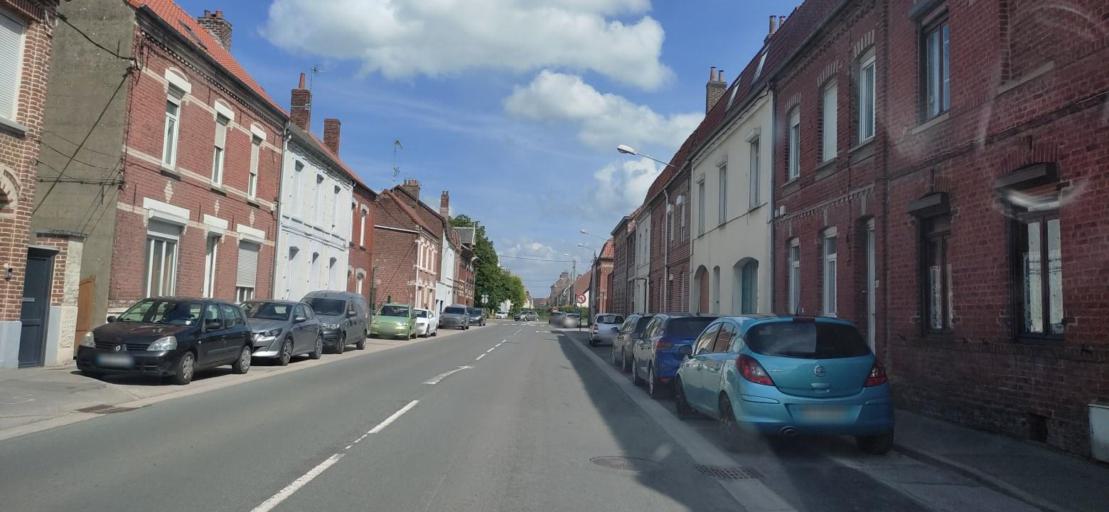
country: FR
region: Nord-Pas-de-Calais
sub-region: Departement du Pas-de-Calais
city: Aire-sur-la-Lys
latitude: 50.6387
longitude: 2.3872
